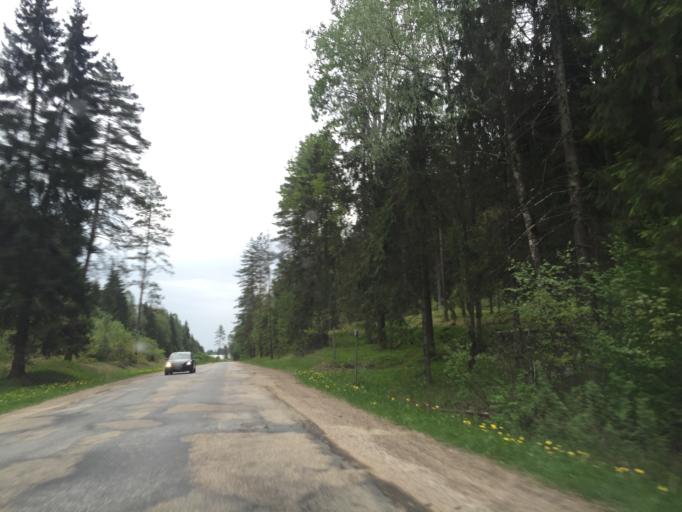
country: LV
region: Ogre
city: Ogre
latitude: 56.8314
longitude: 24.5878
